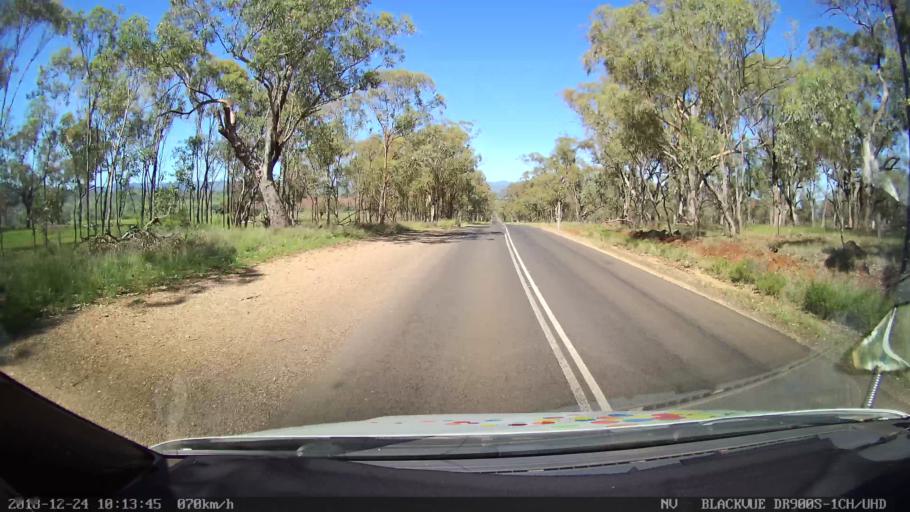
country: AU
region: New South Wales
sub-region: Liverpool Plains
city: Quirindi
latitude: -31.6928
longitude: 150.6376
